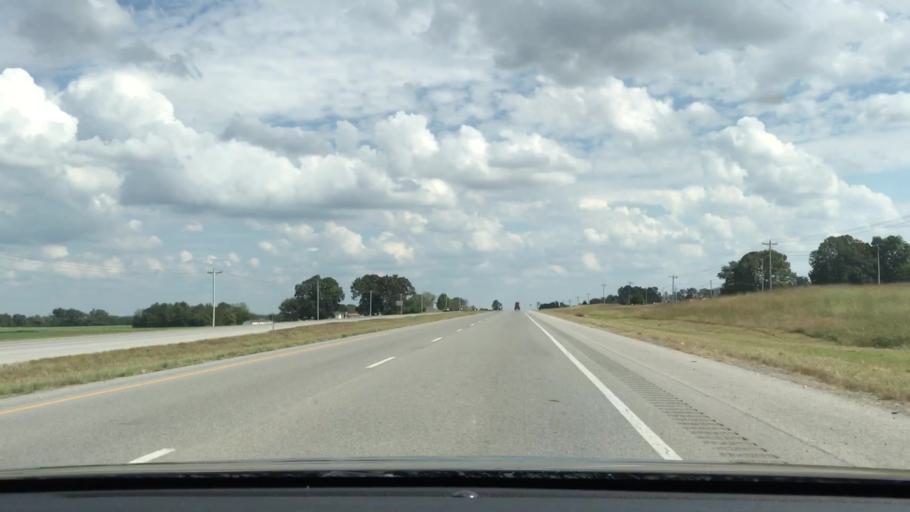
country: US
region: Kentucky
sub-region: Trigg County
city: Cadiz
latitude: 36.8729
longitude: -87.7601
